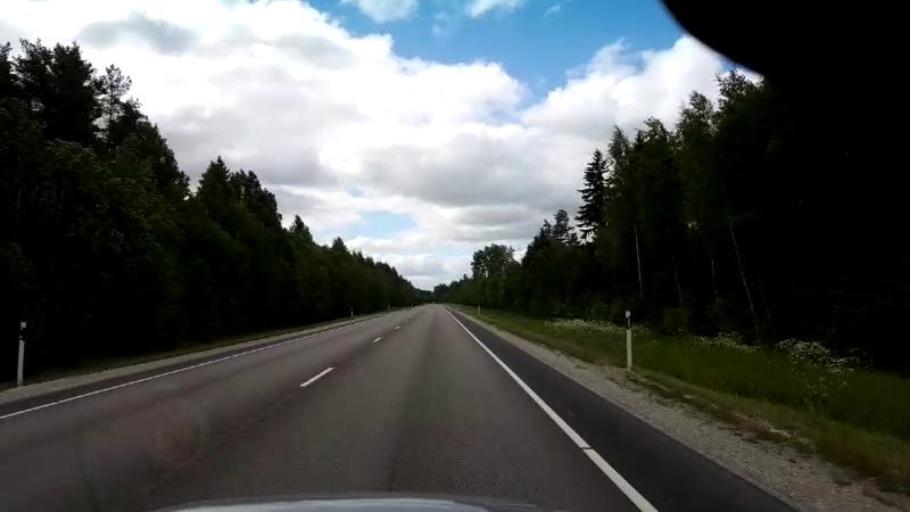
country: EE
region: Paernumaa
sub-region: Halinga vald
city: Parnu-Jaagupi
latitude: 58.7115
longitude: 24.4239
